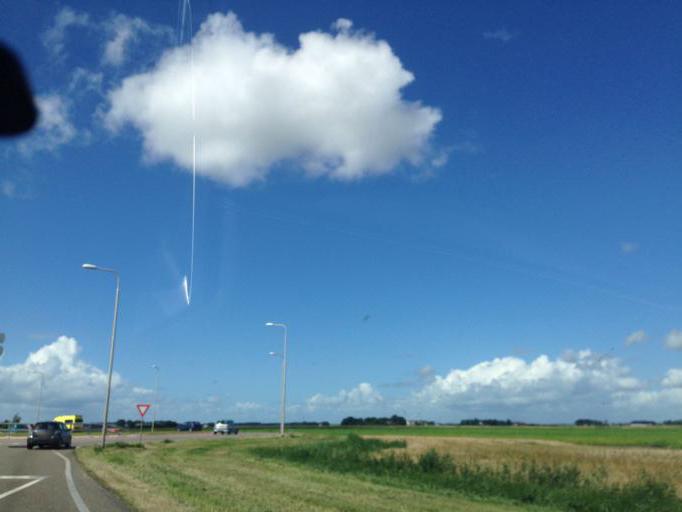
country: NL
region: Flevoland
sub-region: Gemeente Dronten
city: Dronten
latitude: 52.5509
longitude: 5.6956
